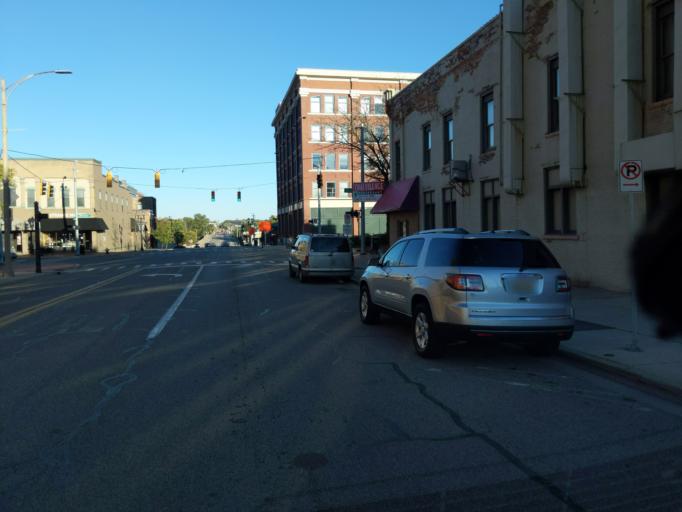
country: US
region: Michigan
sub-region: Ingham County
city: Lansing
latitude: 42.7299
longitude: -84.5529
